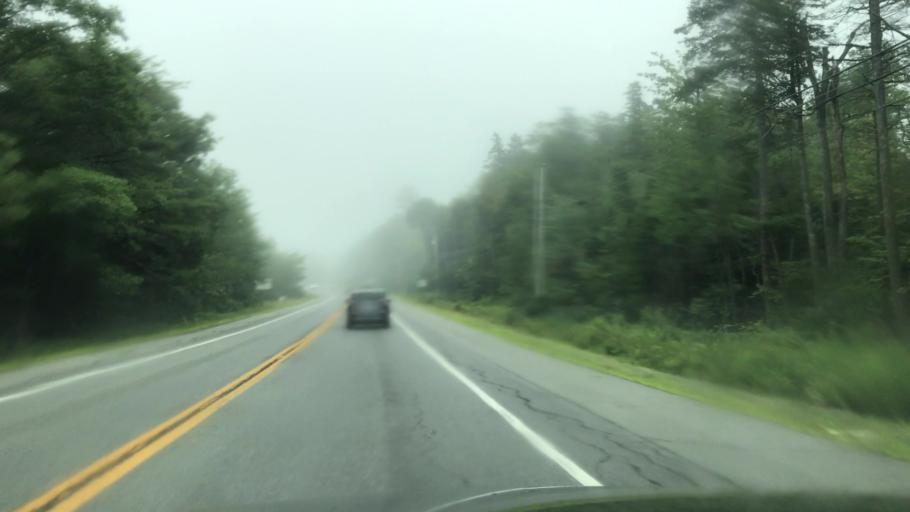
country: US
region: Maine
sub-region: Lincoln County
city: Waldoboro
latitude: 44.0992
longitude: -69.4137
